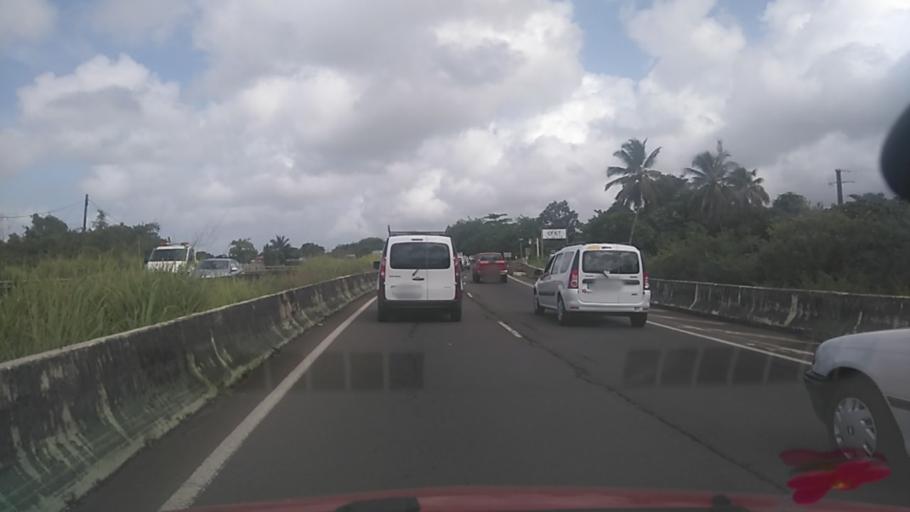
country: MQ
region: Martinique
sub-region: Martinique
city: Le Lamentin
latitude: 14.6249
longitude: -60.9847
